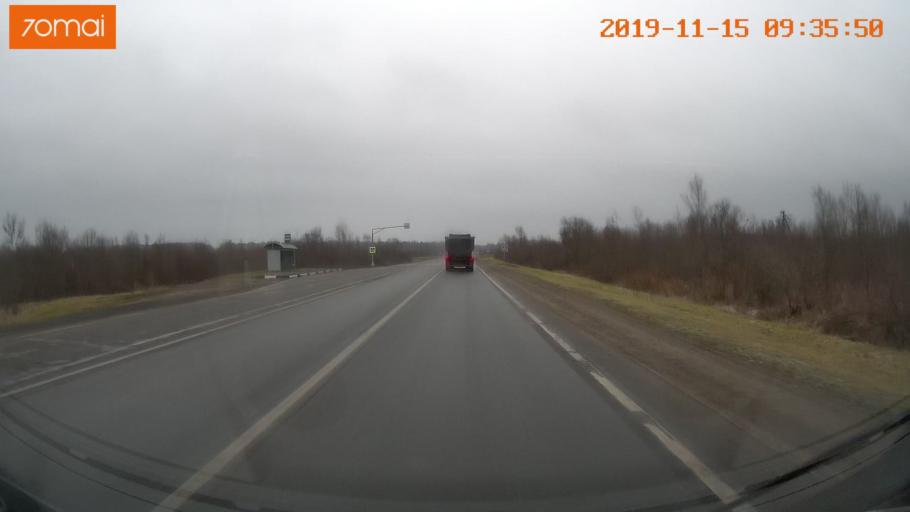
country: RU
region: Vologda
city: Sheksna
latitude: 59.2521
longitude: 38.4071
